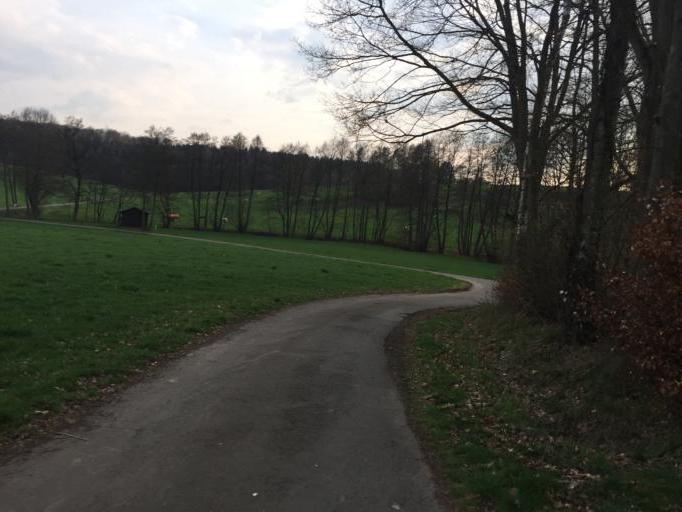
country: DE
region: Hesse
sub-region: Regierungsbezirk Giessen
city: Laubach
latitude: 50.5358
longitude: 9.0054
